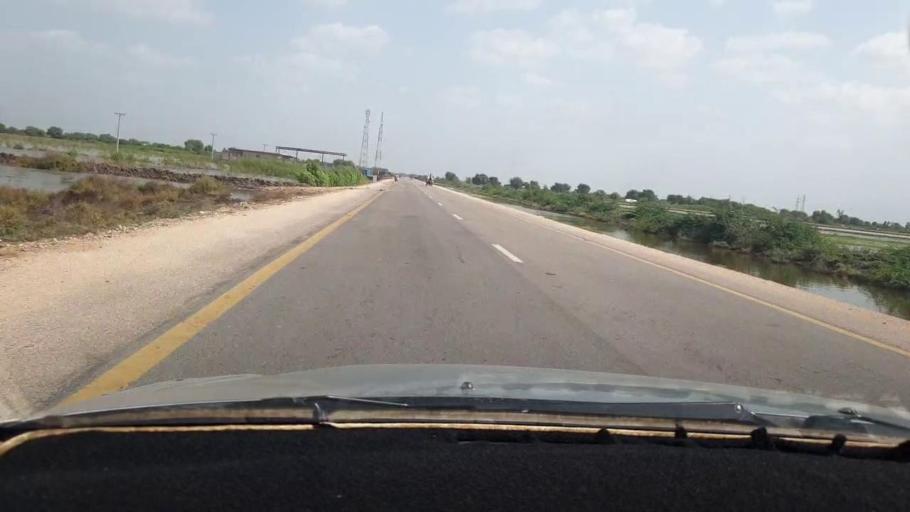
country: PK
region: Sindh
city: Digri
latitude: 25.0303
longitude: 69.2459
